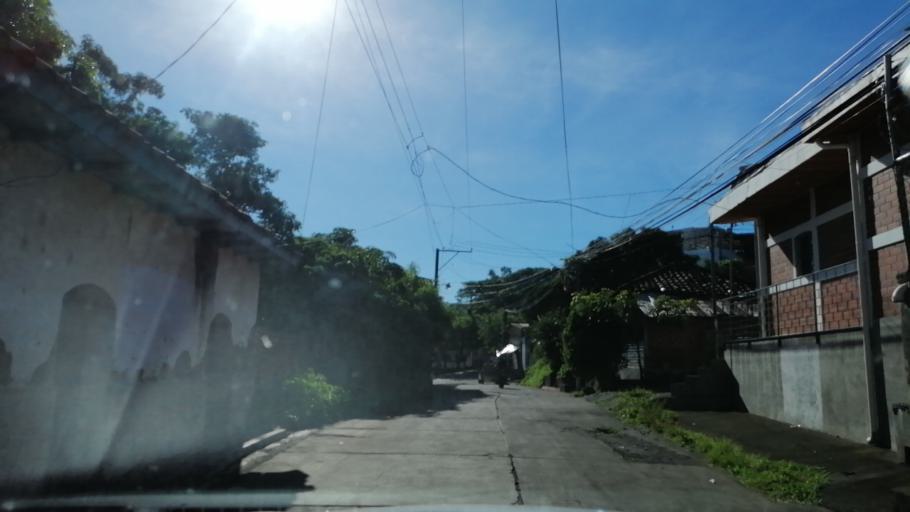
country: SV
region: Morazan
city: Cacaopera
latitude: 13.7726
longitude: -88.0788
